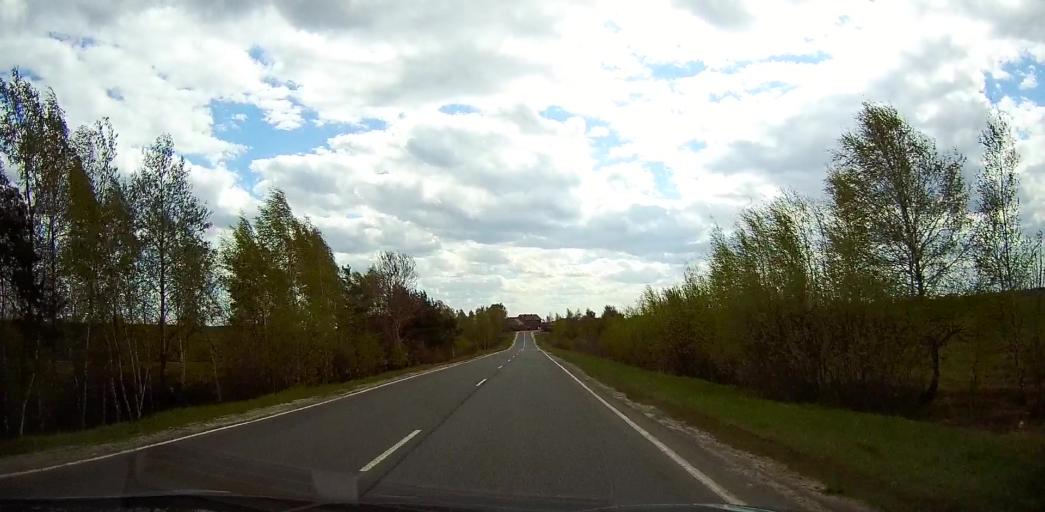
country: RU
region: Moskovskaya
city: Davydovo
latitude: 55.6342
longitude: 38.7462
